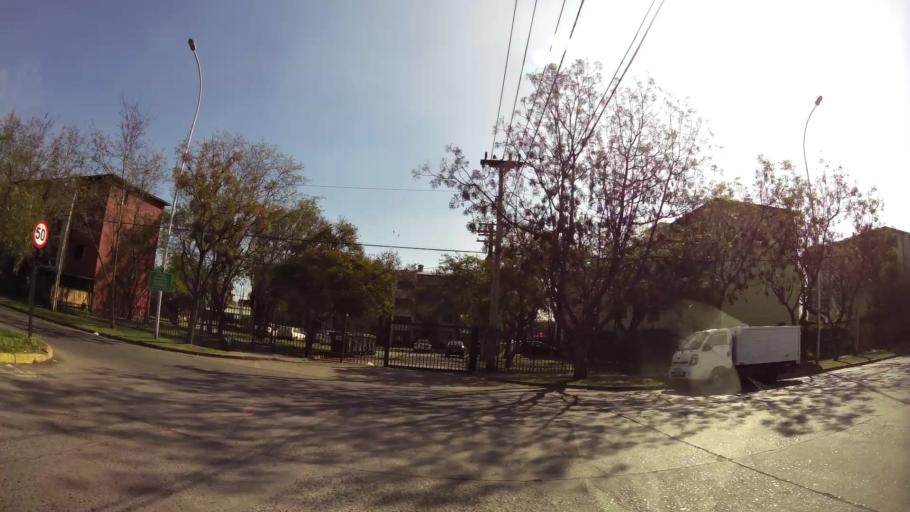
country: CL
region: Santiago Metropolitan
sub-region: Provincia de Santiago
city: Santiago
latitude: -33.4686
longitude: -70.6218
